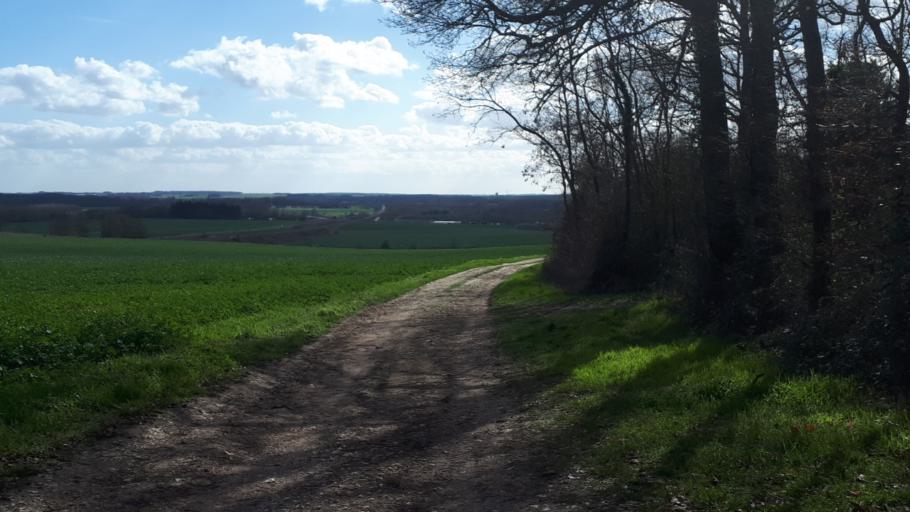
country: FR
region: Centre
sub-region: Departement du Loir-et-Cher
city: Villiers-sur-Loir
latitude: 47.8026
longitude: 1.0100
